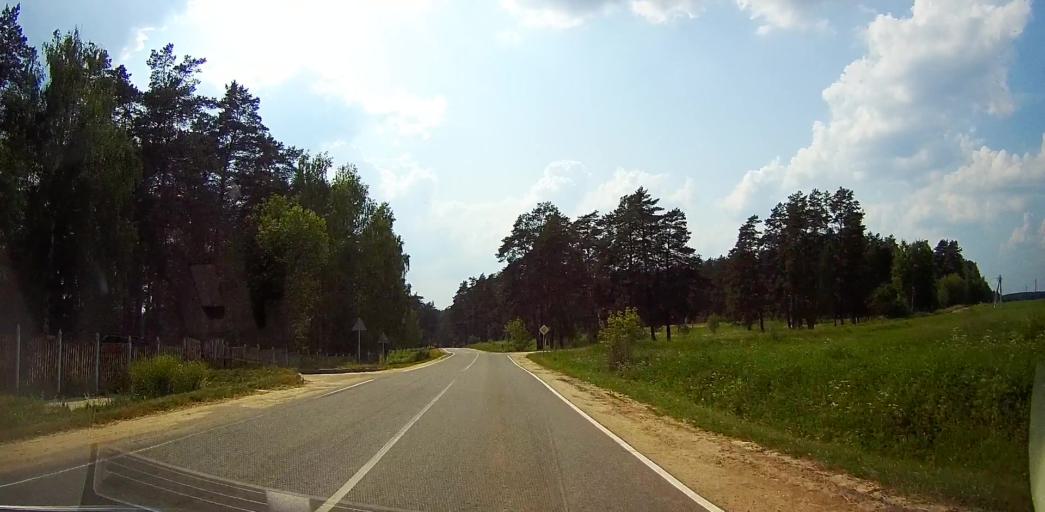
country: RU
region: Moskovskaya
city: Zhilevo
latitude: 55.0557
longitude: 38.0509
